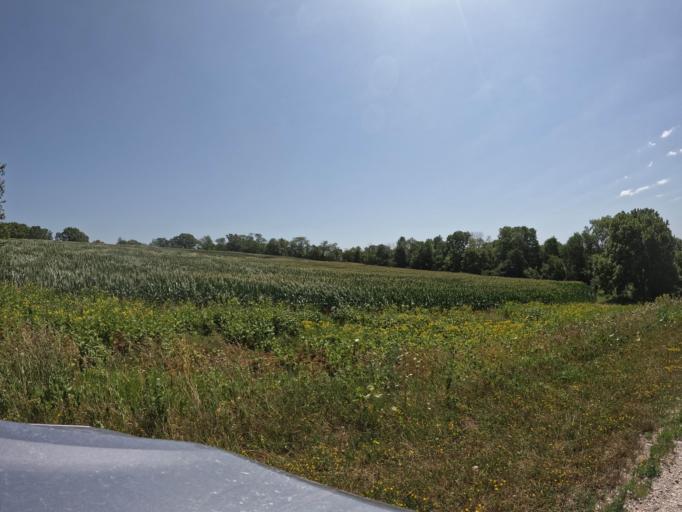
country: US
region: Iowa
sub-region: Henry County
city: Mount Pleasant
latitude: 40.9075
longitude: -91.5544
